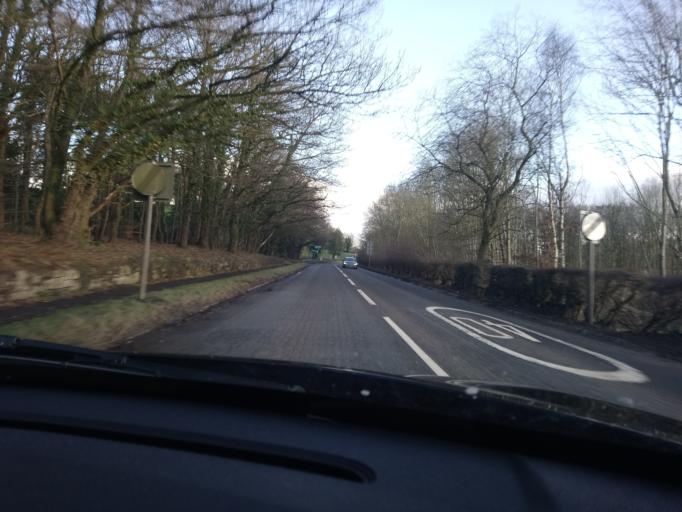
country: GB
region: England
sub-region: Shropshire
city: Ellesmere
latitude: 52.9020
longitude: -2.8793
